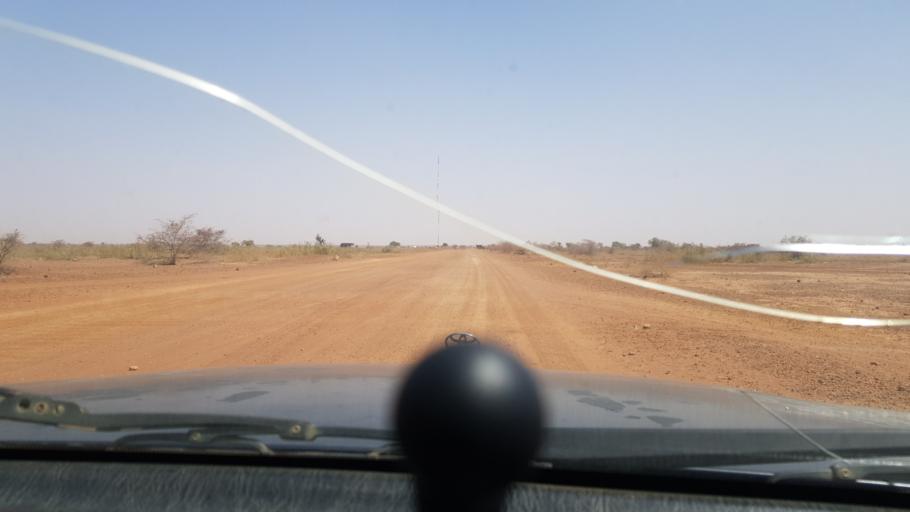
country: NE
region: Niamey
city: Niamey
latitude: 13.4286
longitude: 1.9725
